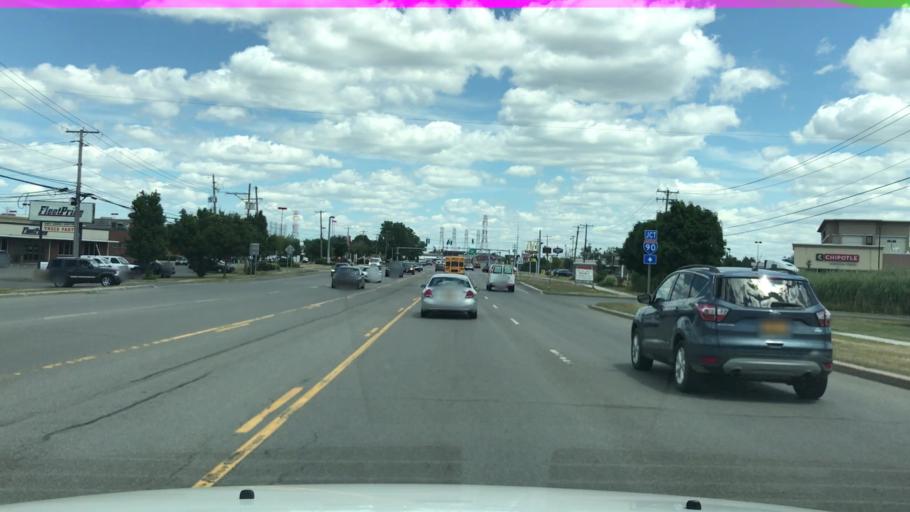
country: US
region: New York
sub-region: Erie County
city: Cheektowaga
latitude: 42.9077
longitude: -78.7757
